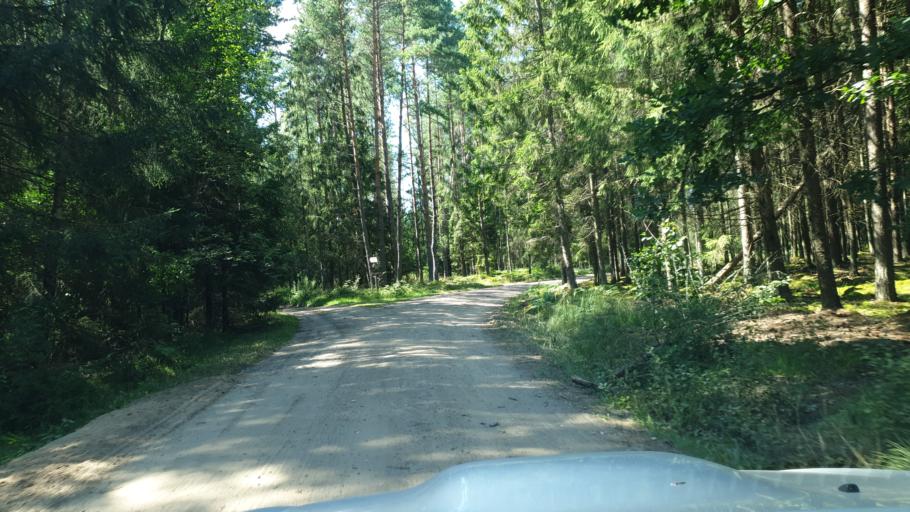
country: LT
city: Sirvintos
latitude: 54.9069
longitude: 24.9454
